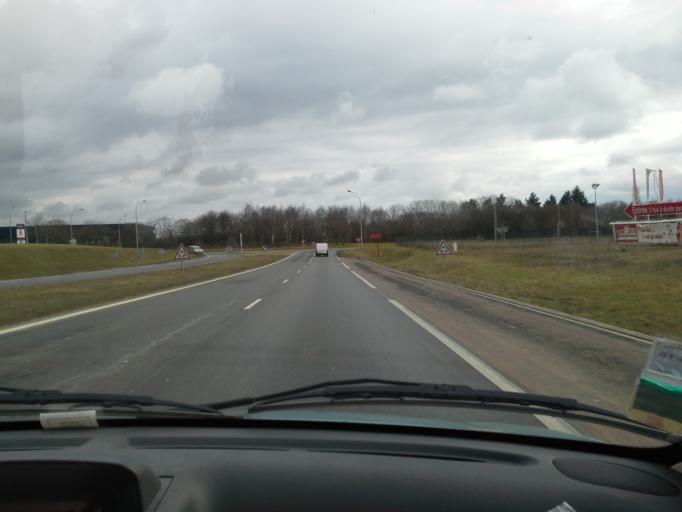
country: FR
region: Centre
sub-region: Departement du Loir-et-Cher
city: Villebarou
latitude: 47.6118
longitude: 1.3369
